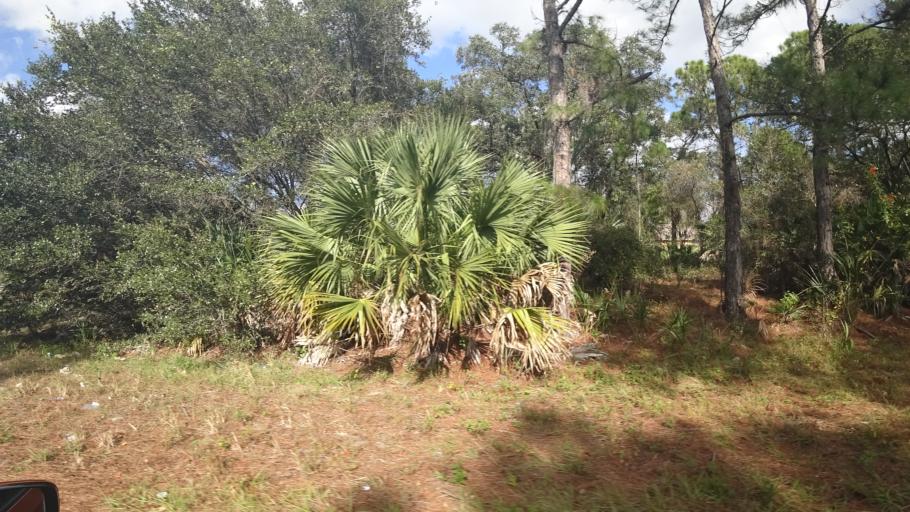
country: US
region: Florida
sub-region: Charlotte County
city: Port Charlotte
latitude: 27.0390
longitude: -82.1370
